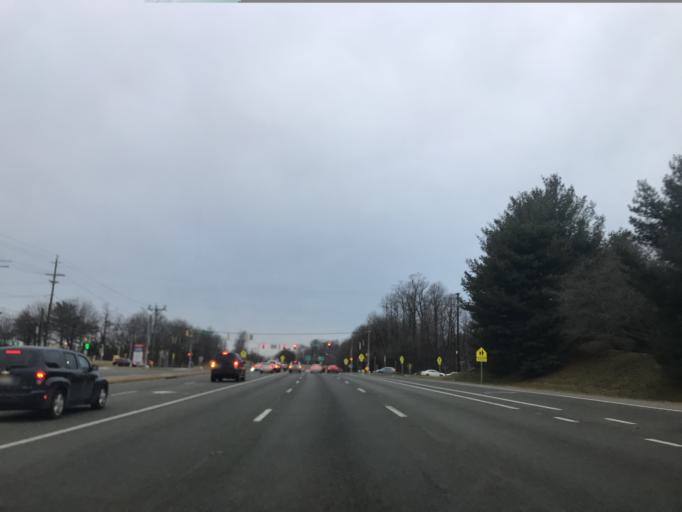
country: US
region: Maryland
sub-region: Prince George's County
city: Largo
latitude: 38.8991
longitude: -76.8211
